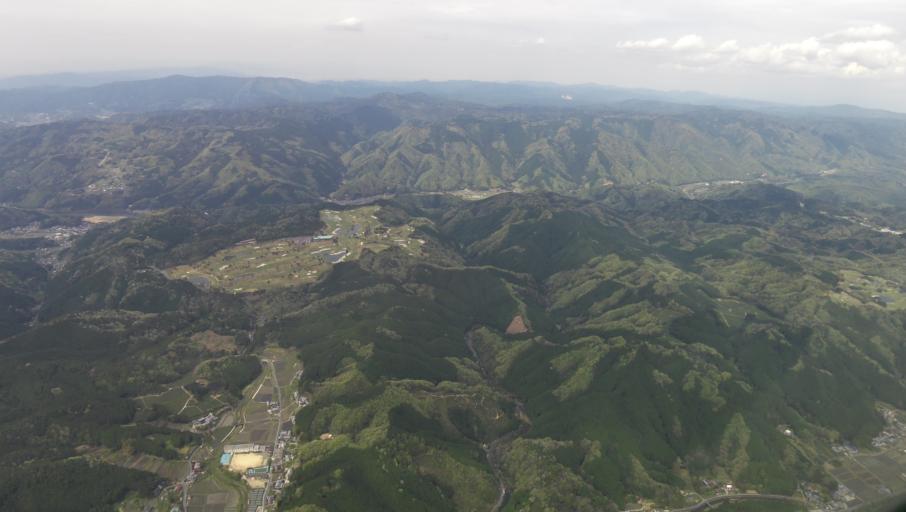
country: JP
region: Nara
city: Nara-shi
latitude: 34.7291
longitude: 135.9553
